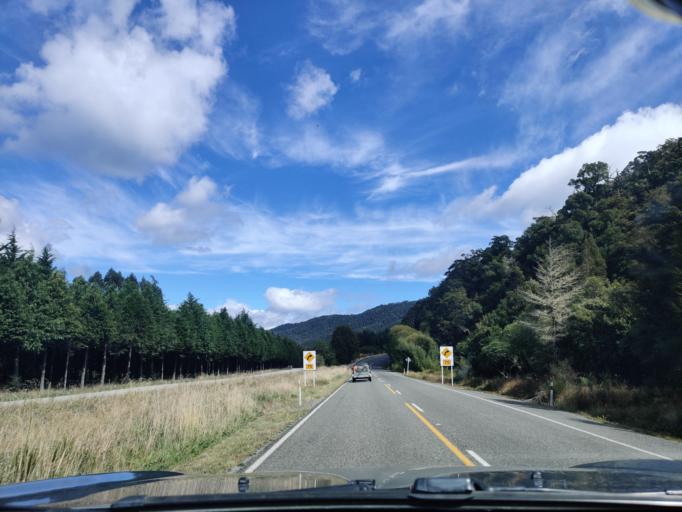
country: NZ
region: Tasman
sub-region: Tasman District
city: Wakefield
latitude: -41.6951
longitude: 172.4789
